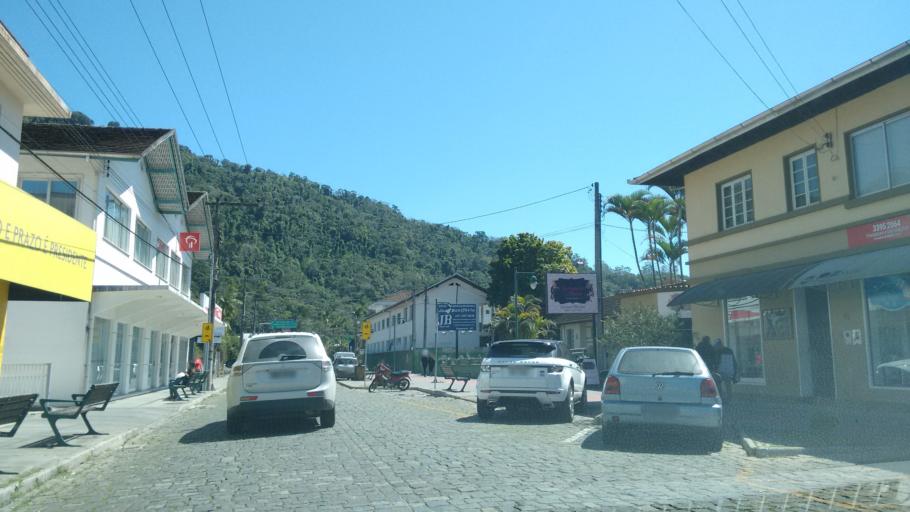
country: BR
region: Santa Catarina
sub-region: Pomerode
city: Pomerode
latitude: -26.7372
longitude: -49.1770
